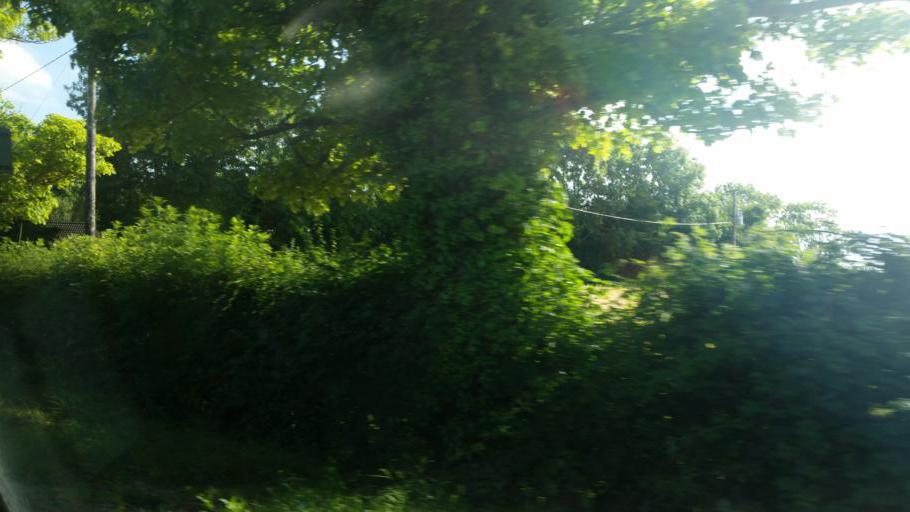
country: IE
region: Leinster
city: Hartstown
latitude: 53.4320
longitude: -6.4277
